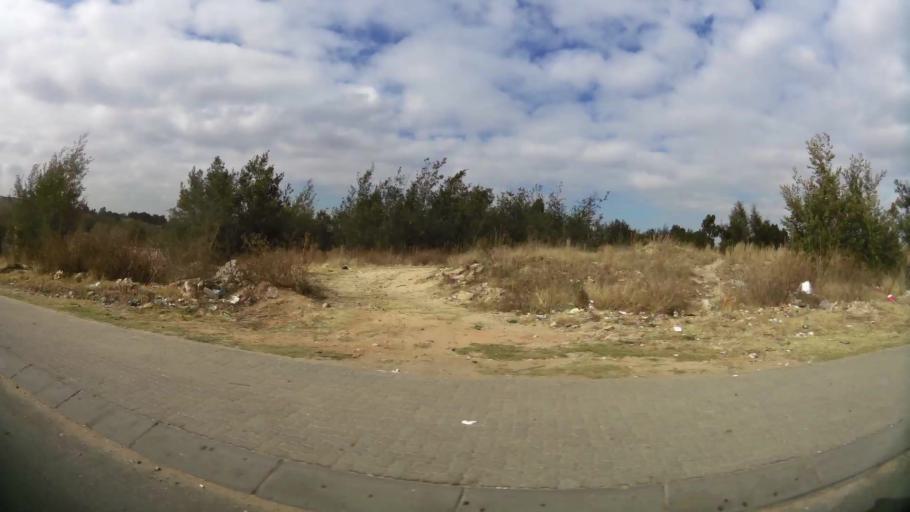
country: ZA
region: Gauteng
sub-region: City of Johannesburg Metropolitan Municipality
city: Roodepoort
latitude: -26.1931
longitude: 27.9045
